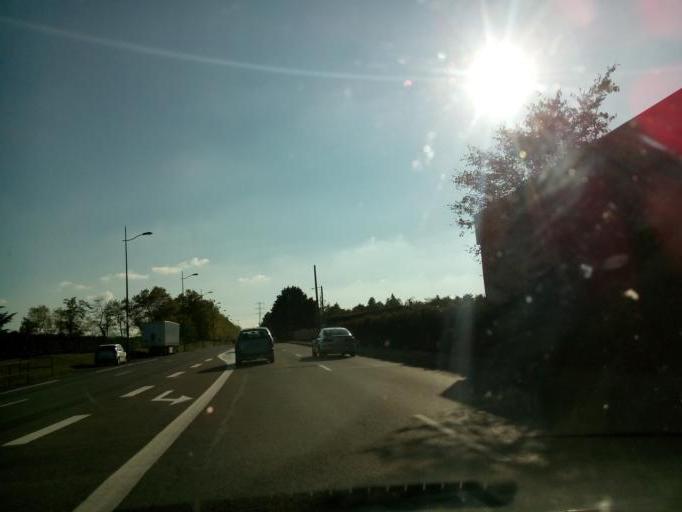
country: FR
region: Rhone-Alpes
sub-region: Departement du Rhone
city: Bron
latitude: 45.7177
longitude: 4.9091
